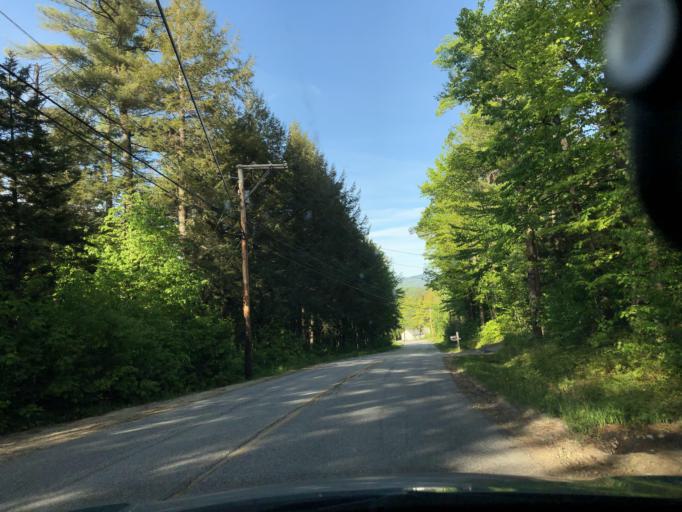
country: US
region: New Hampshire
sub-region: Merrimack County
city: New London
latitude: 43.4231
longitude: -71.9791
